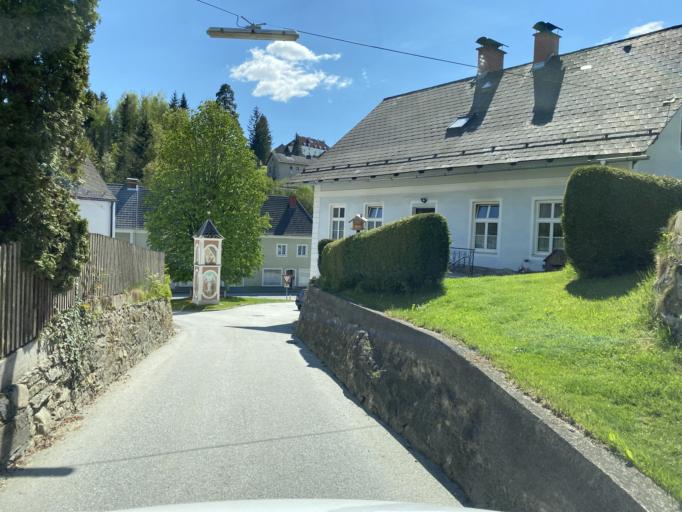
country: AT
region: Styria
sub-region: Politischer Bezirk Weiz
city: Birkfeld
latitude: 47.3574
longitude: 15.6990
